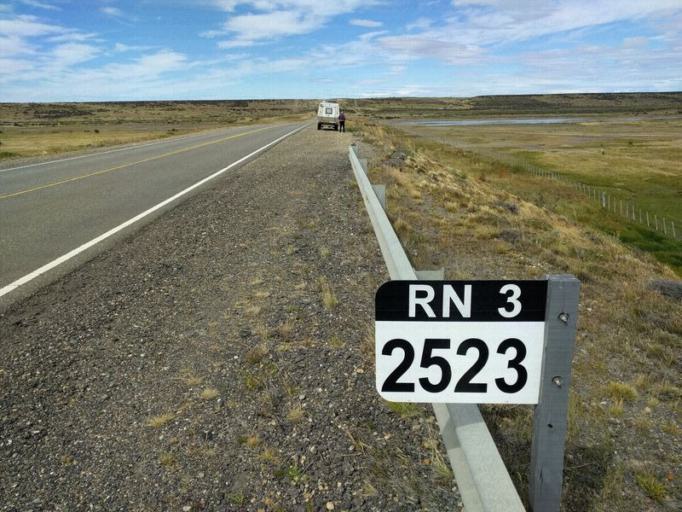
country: AR
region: Santa Cruz
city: Rio Gallegos
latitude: -51.1523
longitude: -69.5257
